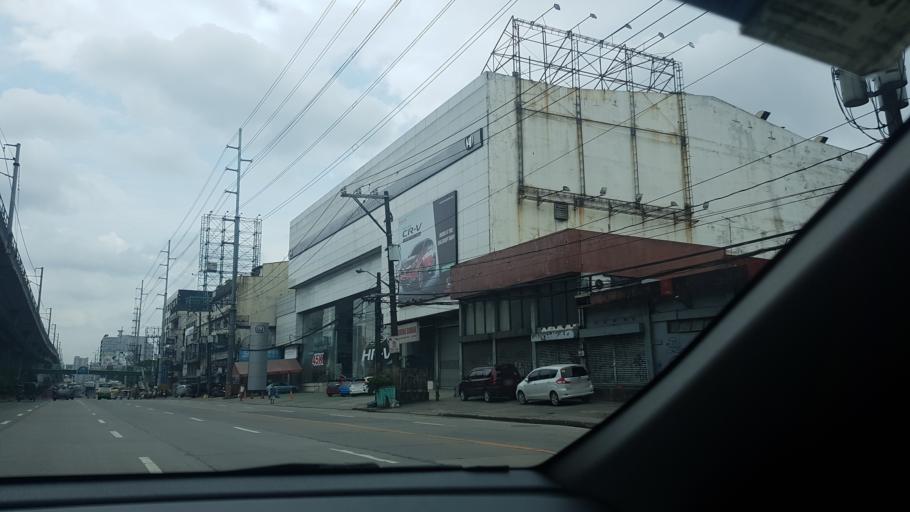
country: PH
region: Calabarzon
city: Del Monte
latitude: 14.6572
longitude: 120.9966
